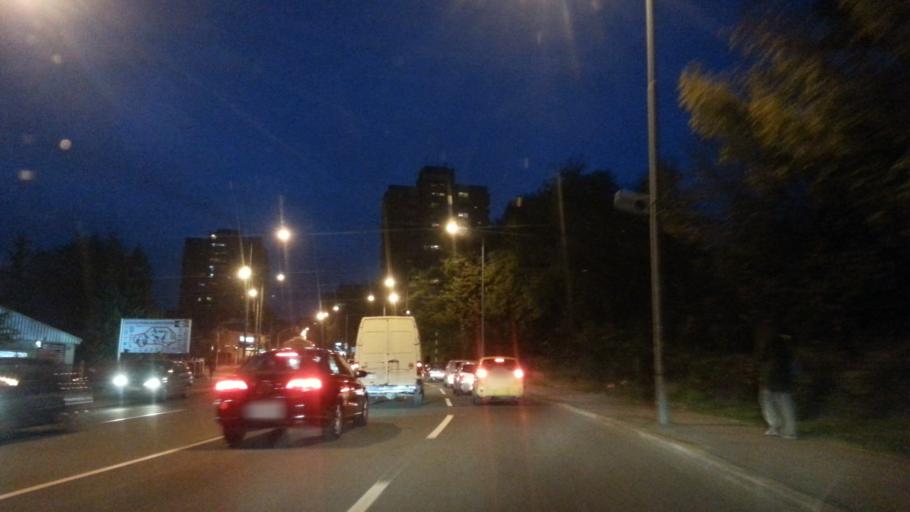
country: RS
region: Central Serbia
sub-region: Belgrade
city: Rakovica
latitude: 44.7455
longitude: 20.4401
